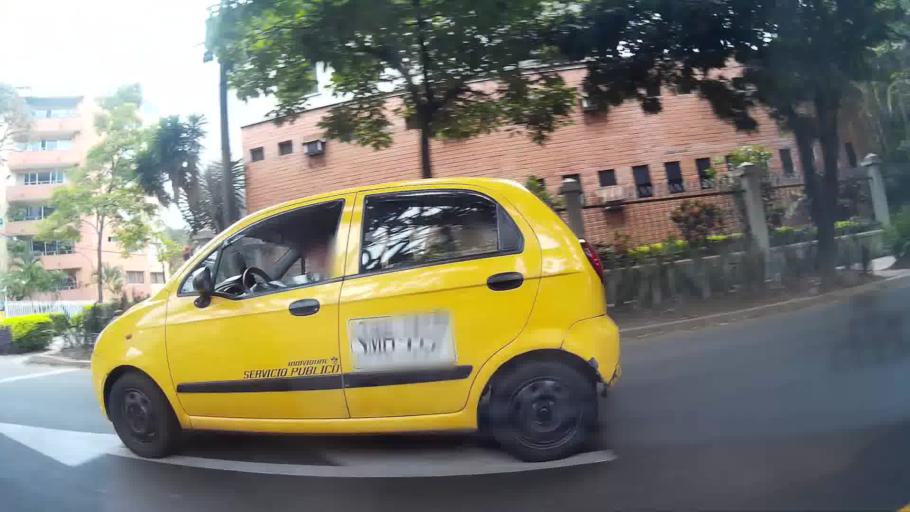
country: CO
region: Antioquia
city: Medellin
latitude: 6.2470
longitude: -75.5969
